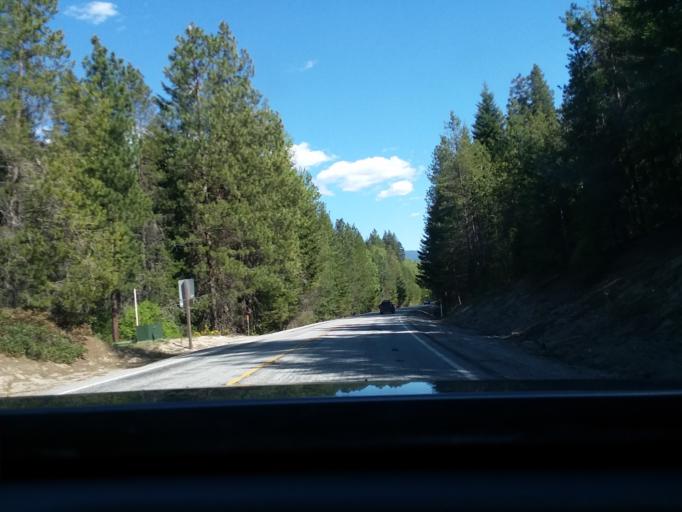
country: US
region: Washington
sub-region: Chelan County
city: Leavenworth
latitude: 47.7999
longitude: -120.6723
